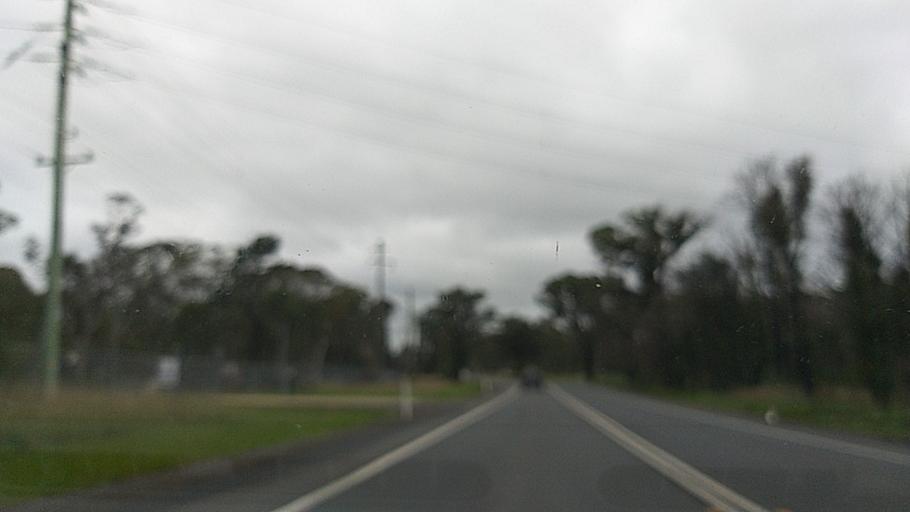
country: AU
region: New South Wales
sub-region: Penrith Municipality
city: Werrington Downs
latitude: -33.6851
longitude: 150.7359
